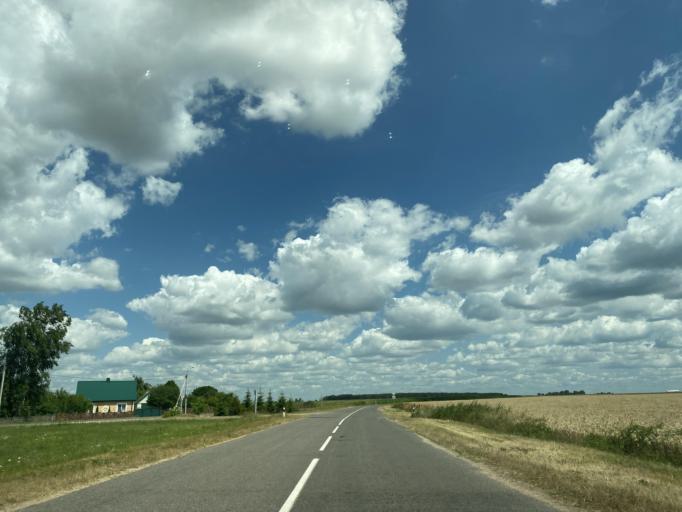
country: BY
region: Brest
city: Ivanava
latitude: 52.1718
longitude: 25.5615
